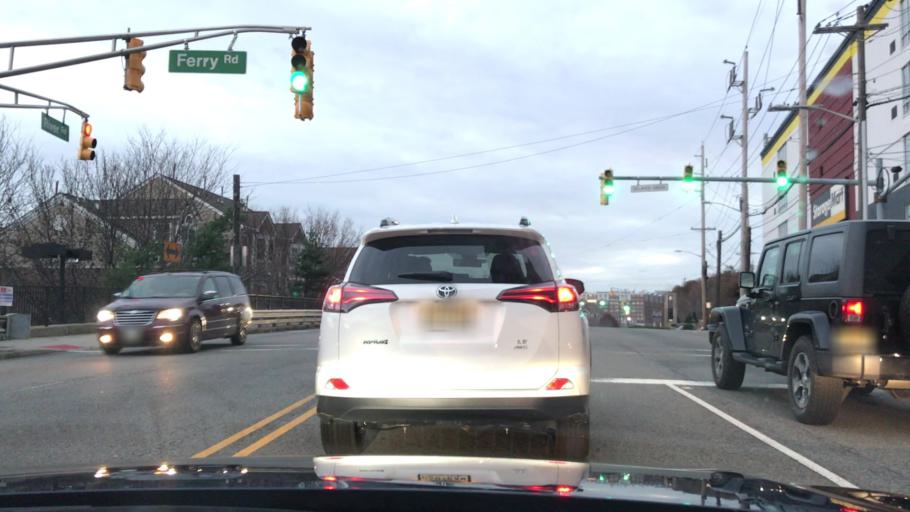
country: US
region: New Jersey
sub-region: Hudson County
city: Guttenberg
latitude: 40.7897
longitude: -73.9997
